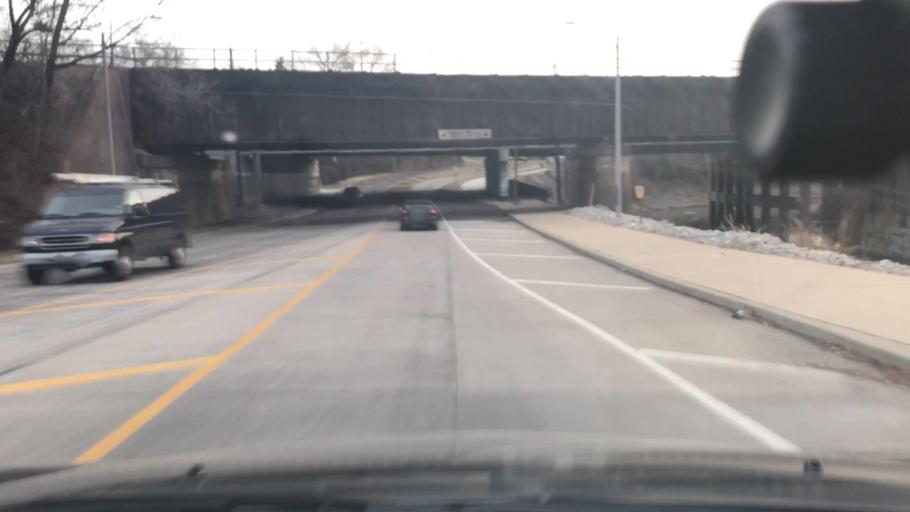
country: US
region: Missouri
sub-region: Saint Louis County
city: Maplewood
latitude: 38.6011
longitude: -90.3154
